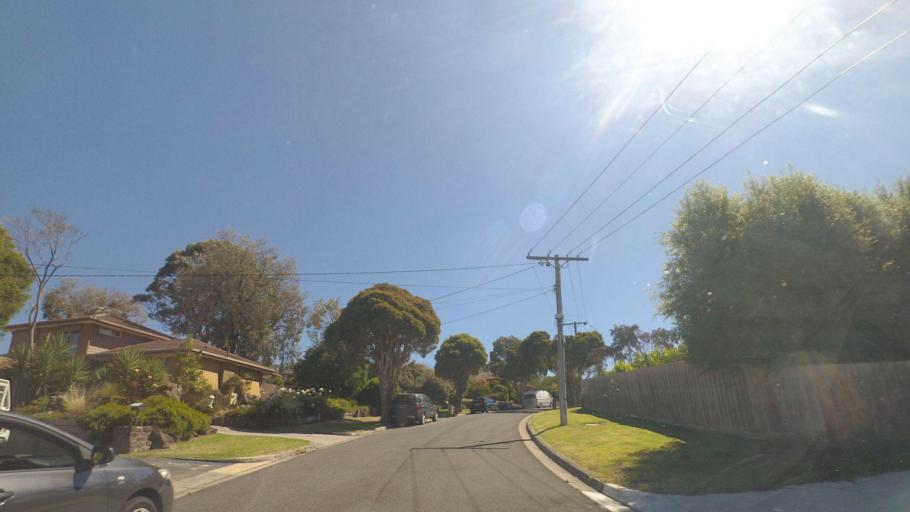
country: AU
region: Victoria
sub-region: Yarra Ranges
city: Chirnside Park
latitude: -37.7470
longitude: 145.3287
